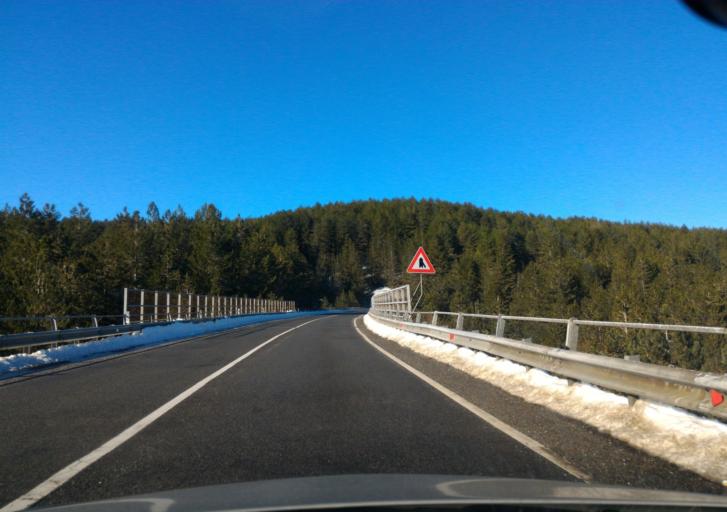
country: IT
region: Calabria
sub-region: Provincia di Cosenza
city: Celico
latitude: 39.3352
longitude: 16.4218
